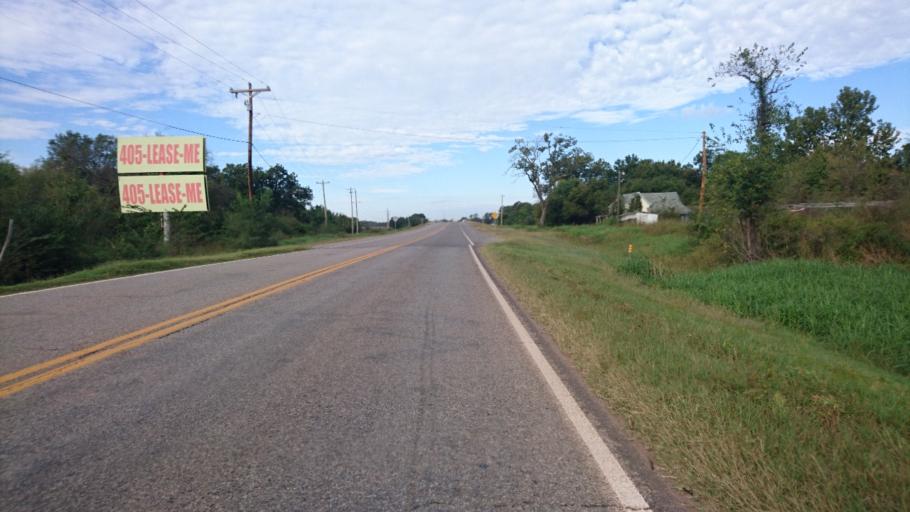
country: US
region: Oklahoma
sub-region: Lincoln County
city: Chandler
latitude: 35.6811
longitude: -97.0056
